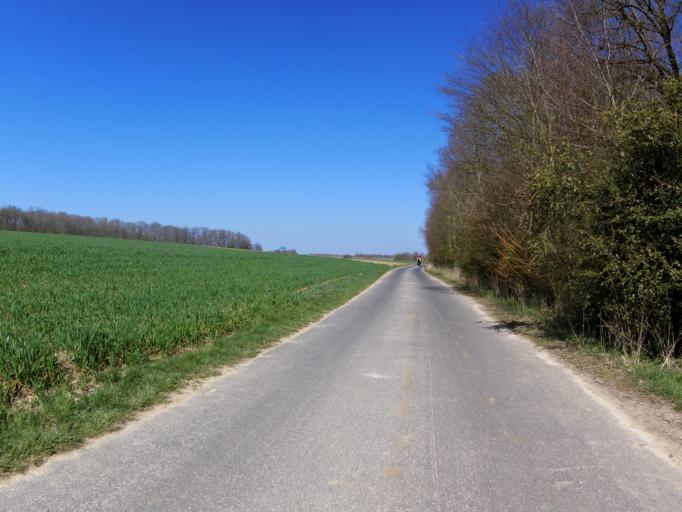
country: DE
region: Bavaria
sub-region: Regierungsbezirk Unterfranken
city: Biebelried
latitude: 49.7714
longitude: 10.0854
